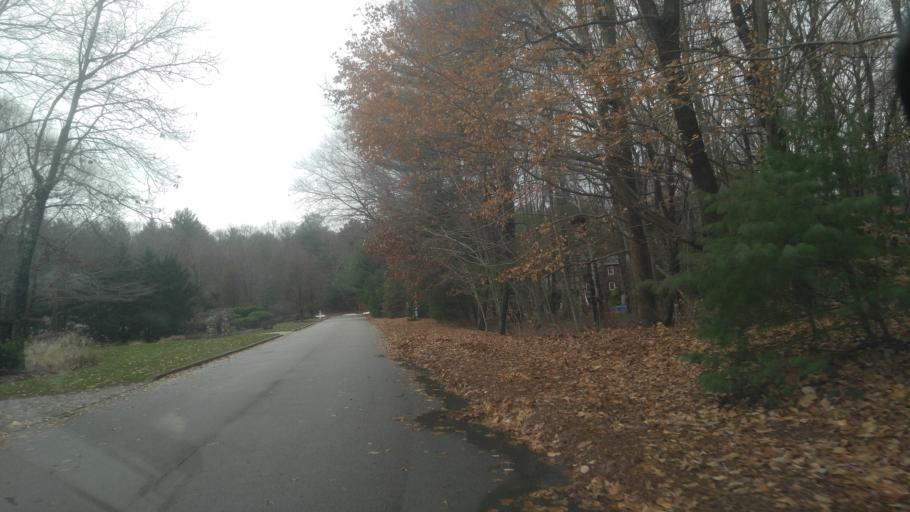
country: US
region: Rhode Island
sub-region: Kent County
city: West Warwick
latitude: 41.6462
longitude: -71.5395
